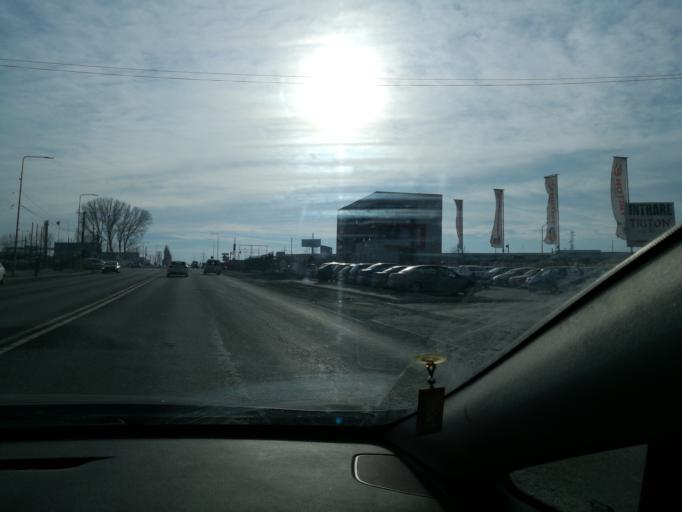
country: RO
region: Constanta
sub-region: Municipiul Constanta
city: Constanta
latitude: 44.1945
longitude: 28.6034
